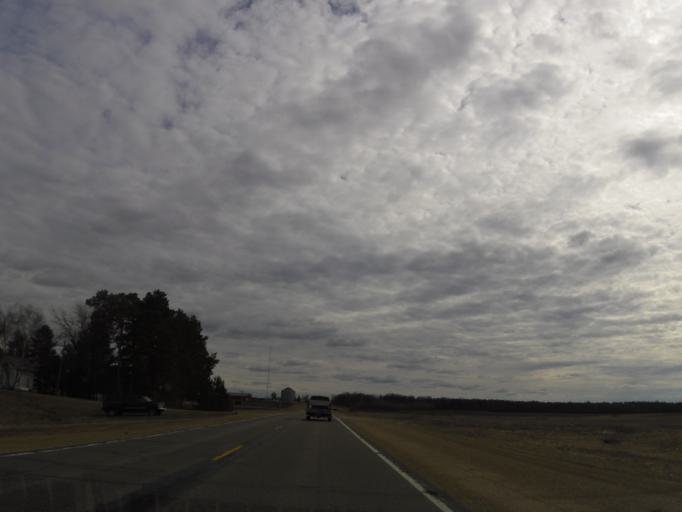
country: US
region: Iowa
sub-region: Howard County
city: Cresco
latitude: 43.2920
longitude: -92.2989
